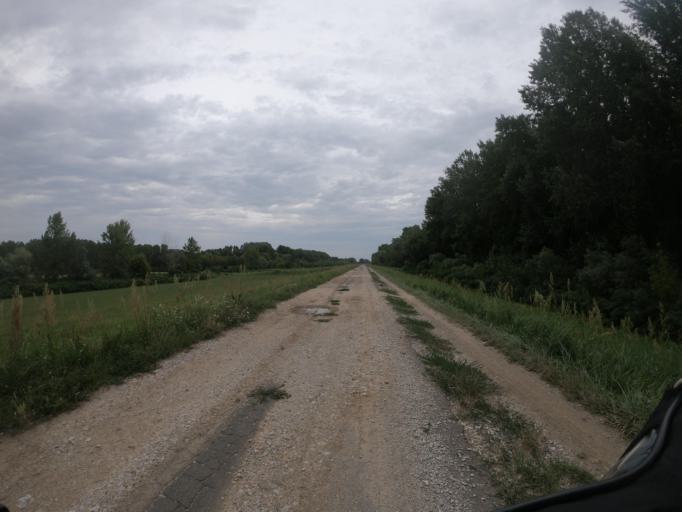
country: HU
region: Hajdu-Bihar
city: Egyek
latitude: 47.6860
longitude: 20.8811
